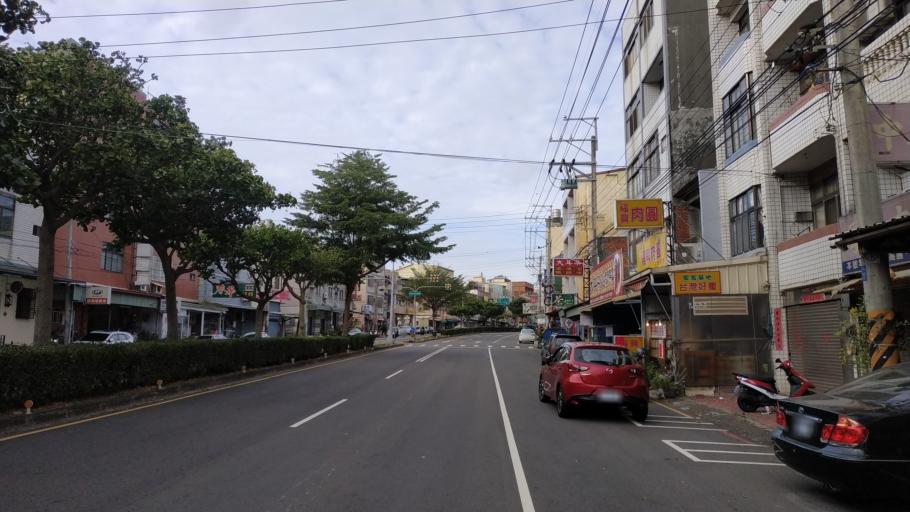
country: TW
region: Taiwan
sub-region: Taichung City
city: Taichung
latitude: 24.2216
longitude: 120.5692
